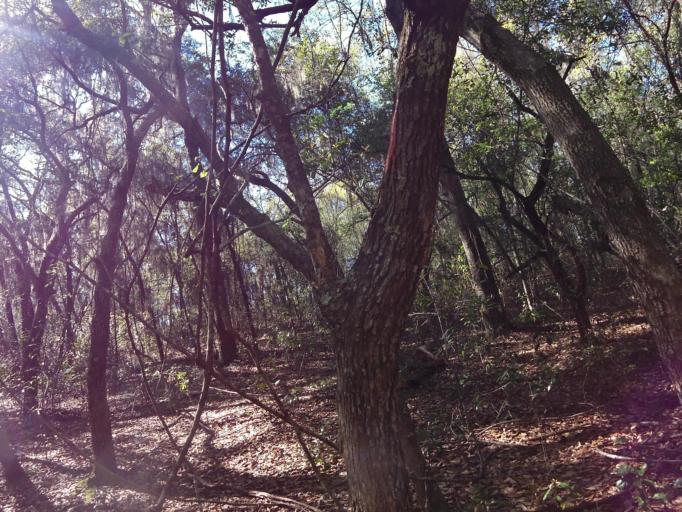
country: US
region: Florida
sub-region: Clay County
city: Keystone Heights
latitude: 29.8294
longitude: -82.0198
